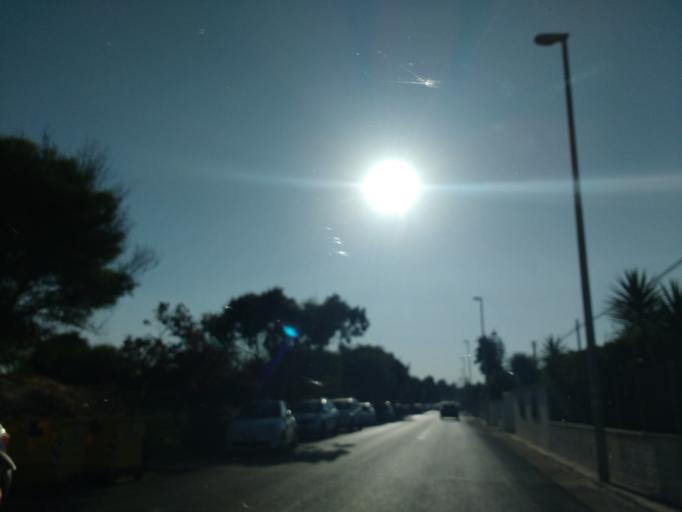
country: IT
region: Sicily
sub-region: Ragusa
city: Pozzallo
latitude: 36.7290
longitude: 14.9008
